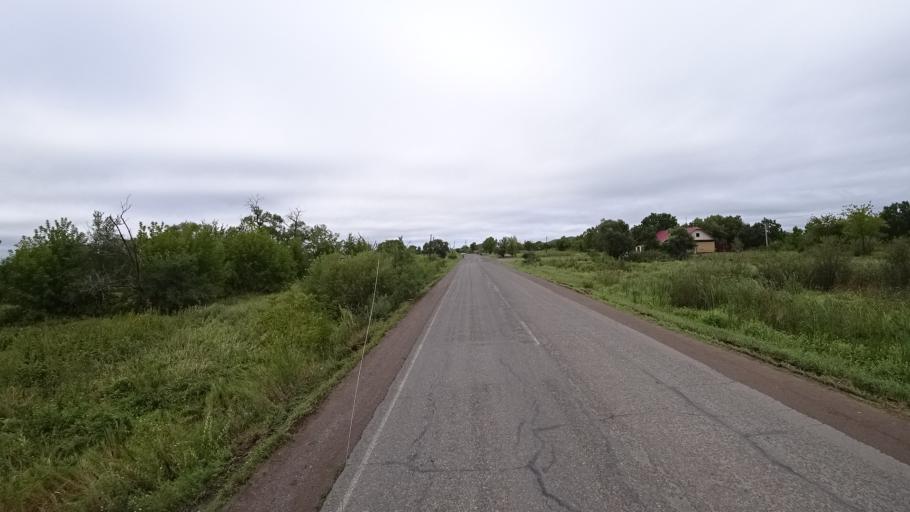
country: RU
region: Primorskiy
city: Monastyrishche
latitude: 44.1936
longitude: 132.4802
